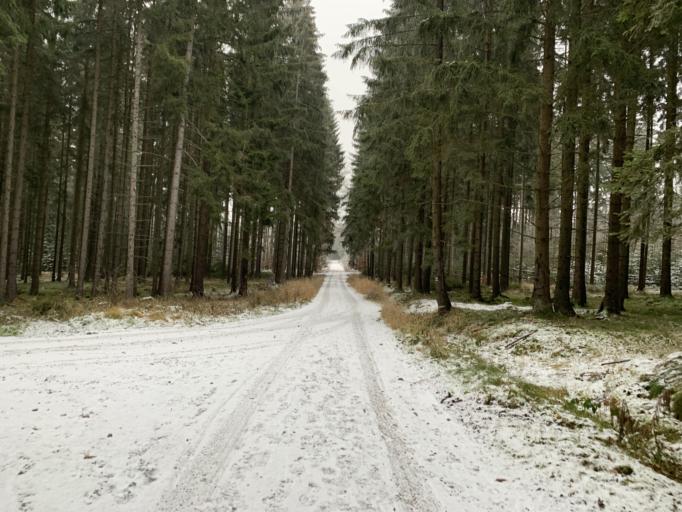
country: CZ
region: Central Bohemia
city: Rozmital pod Tremsinem
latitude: 49.5790
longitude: 13.8112
